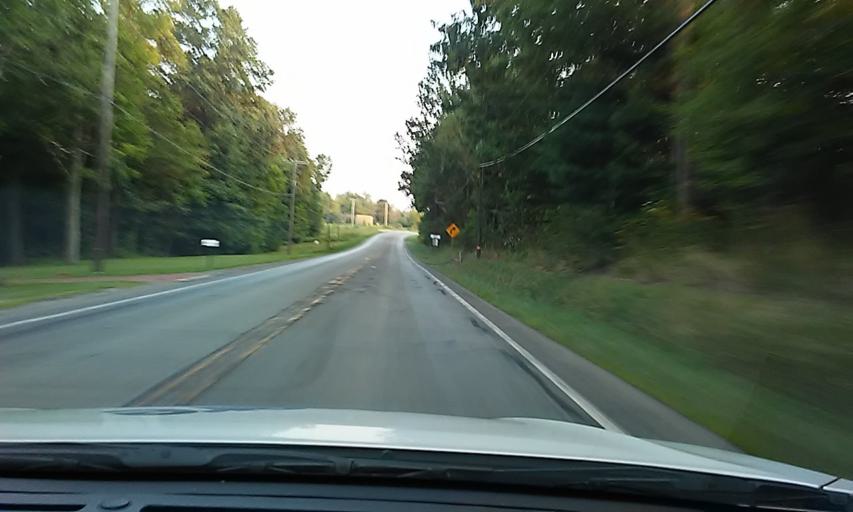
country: US
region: Pennsylvania
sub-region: Clarion County
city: Marianne
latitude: 41.2906
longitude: -79.3836
